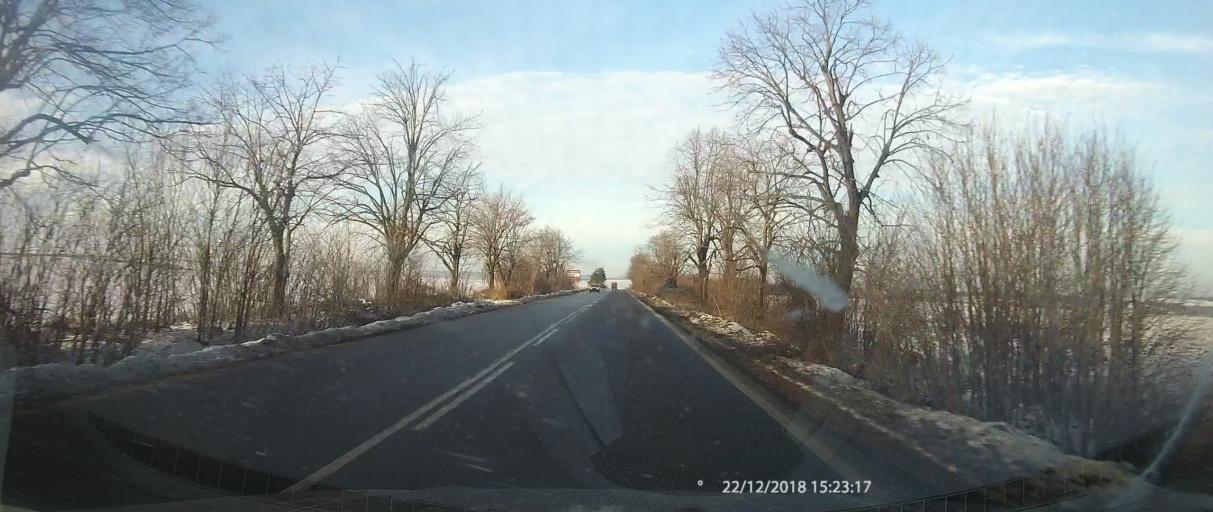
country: BG
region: Ruse
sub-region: Obshtina Ivanovo
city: Ivanovo
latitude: 43.7190
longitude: 25.9203
